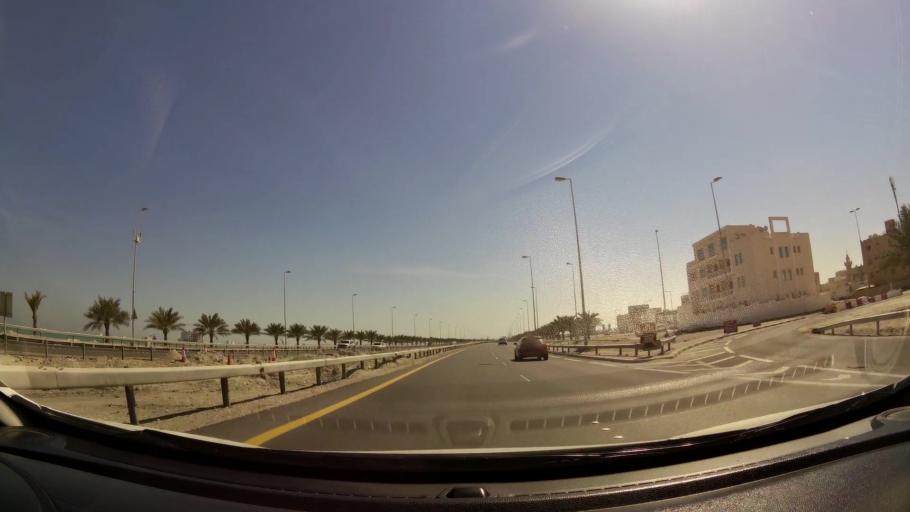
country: BH
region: Muharraq
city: Al Hadd
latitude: 26.2677
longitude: 50.6619
